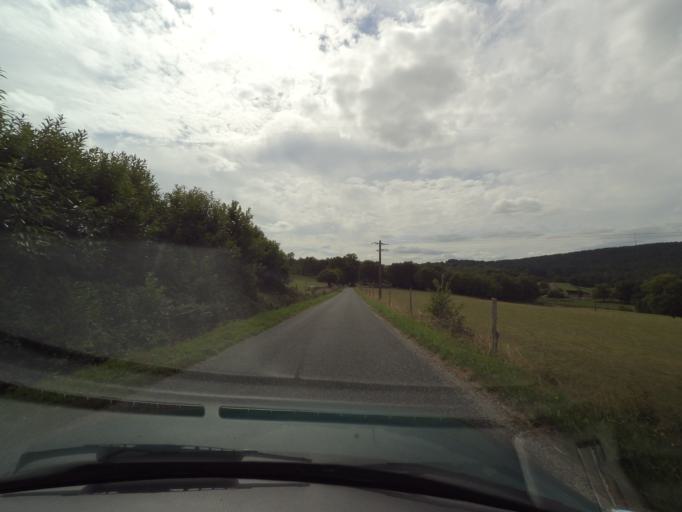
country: FR
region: Limousin
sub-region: Departement de la Haute-Vienne
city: Ladignac-le-Long
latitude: 45.6477
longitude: 1.1063
